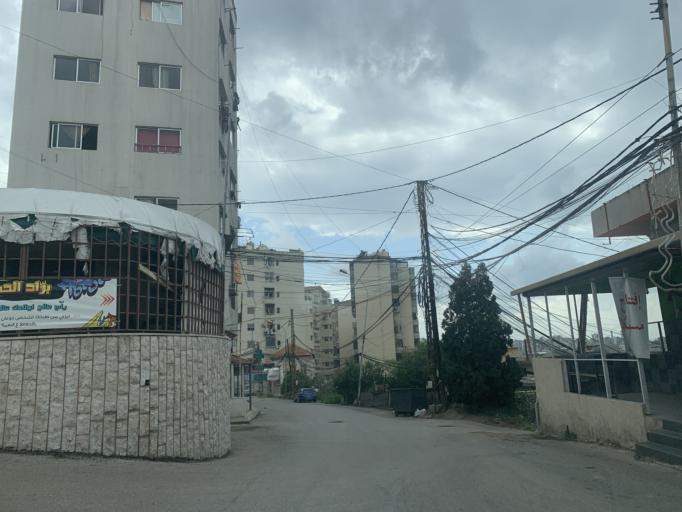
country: LB
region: Mont-Liban
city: Djounie
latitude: 33.9872
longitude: 35.6434
